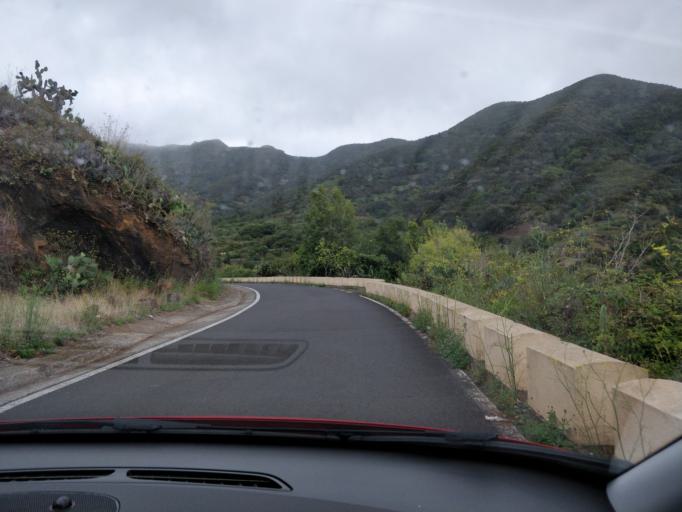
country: ES
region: Canary Islands
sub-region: Provincia de Santa Cruz de Tenerife
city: Tanque
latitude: 28.3256
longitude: -16.8457
